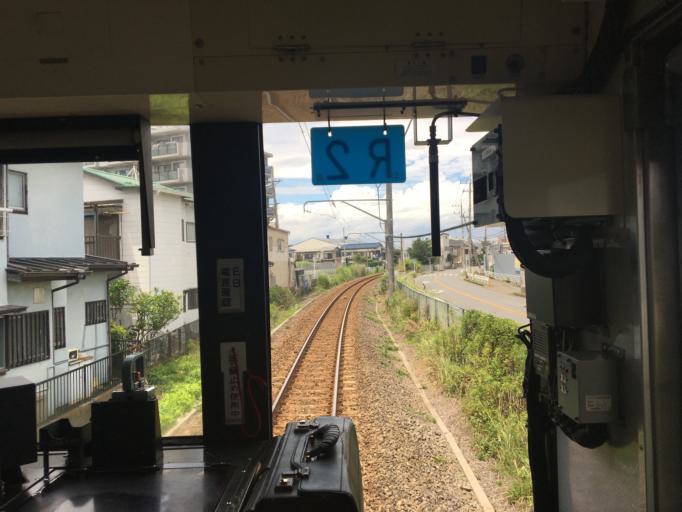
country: JP
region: Kanagawa
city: Atsugi
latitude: 35.4094
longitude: 139.3786
